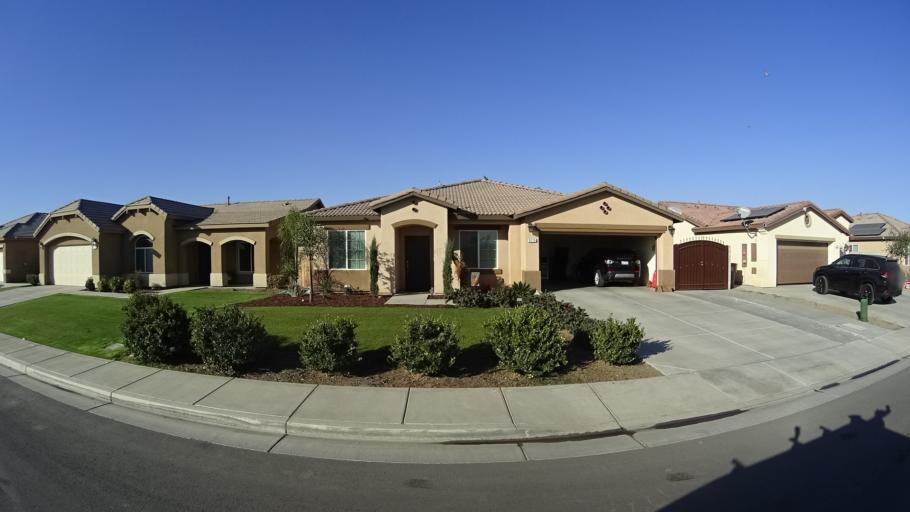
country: US
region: California
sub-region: Kern County
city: Greenfield
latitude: 35.2719
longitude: -119.0259
